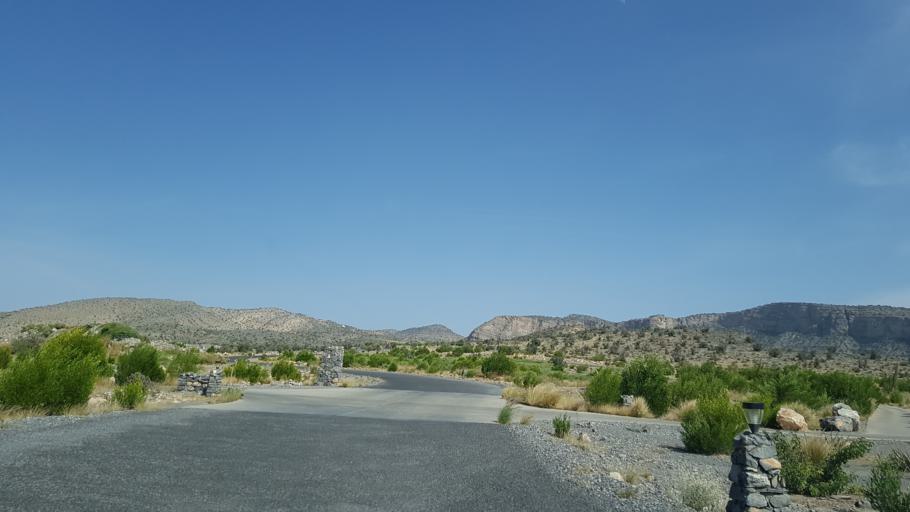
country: OM
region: Al Batinah
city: Bayt al `Awabi
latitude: 23.1428
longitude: 57.5334
